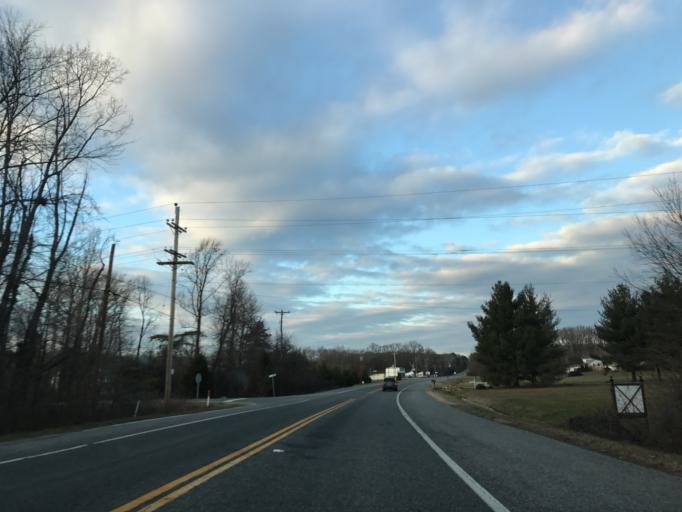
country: US
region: Maryland
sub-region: Cecil County
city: Charlestown
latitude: 39.5582
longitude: -75.9501
